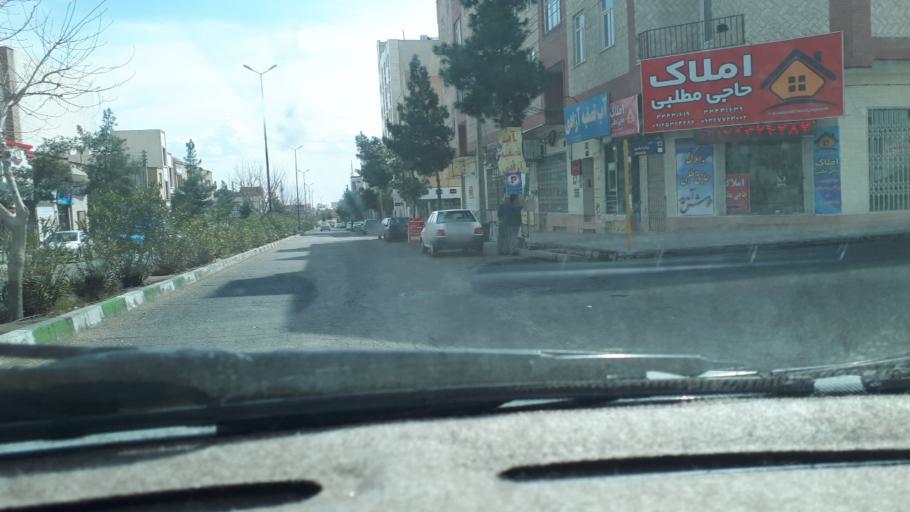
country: IR
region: Semnan
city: Semnan
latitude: 35.5860
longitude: 53.3805
